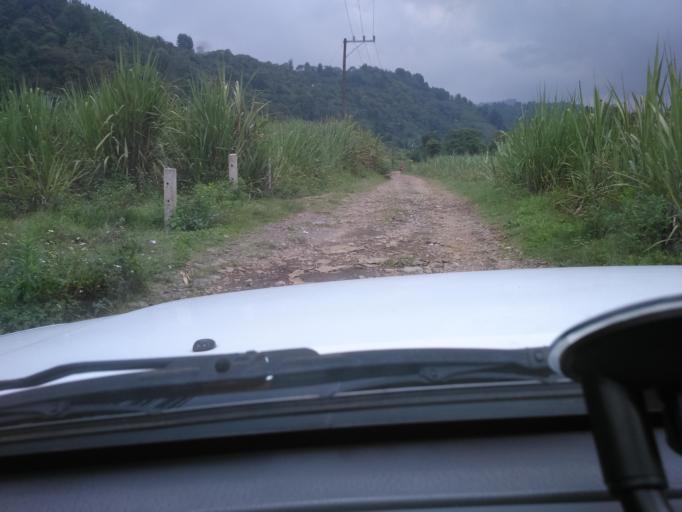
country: MX
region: Veracruz
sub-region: Mariano Escobedo
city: Chicola
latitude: 18.9113
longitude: -97.1114
